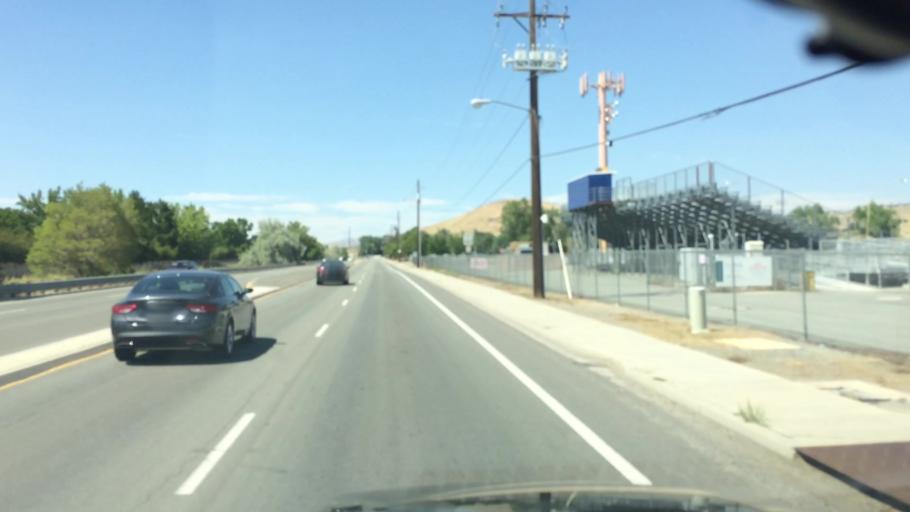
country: US
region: Nevada
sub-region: Washoe County
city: Sparks
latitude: 39.5573
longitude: -119.7244
